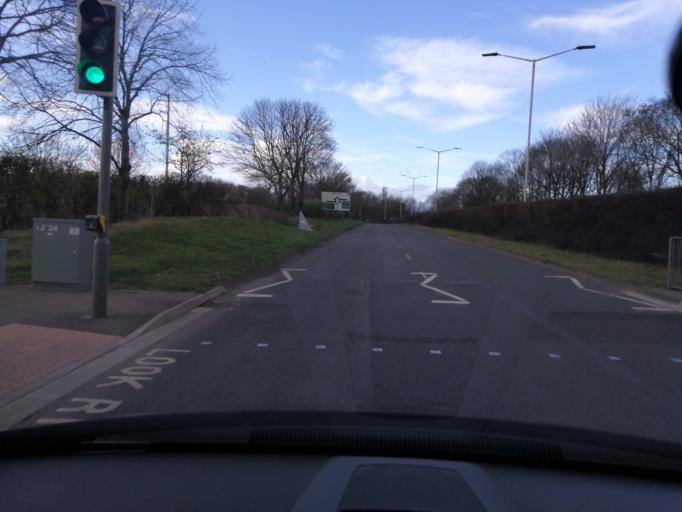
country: GB
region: England
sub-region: Peterborough
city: Peterborough
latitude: 52.5938
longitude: -0.2684
